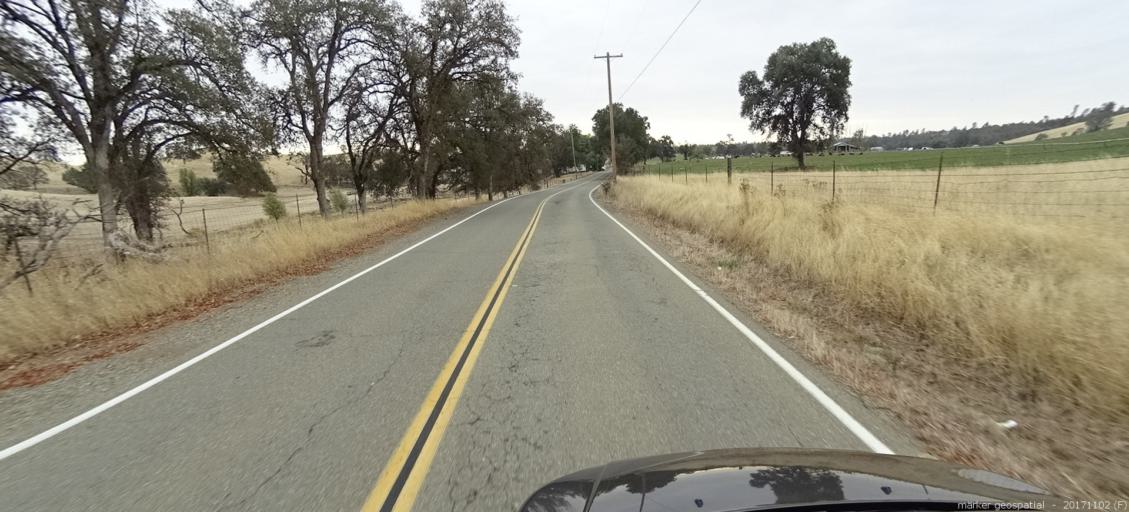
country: US
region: California
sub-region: Shasta County
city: Bella Vista
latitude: 40.6603
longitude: -122.2423
